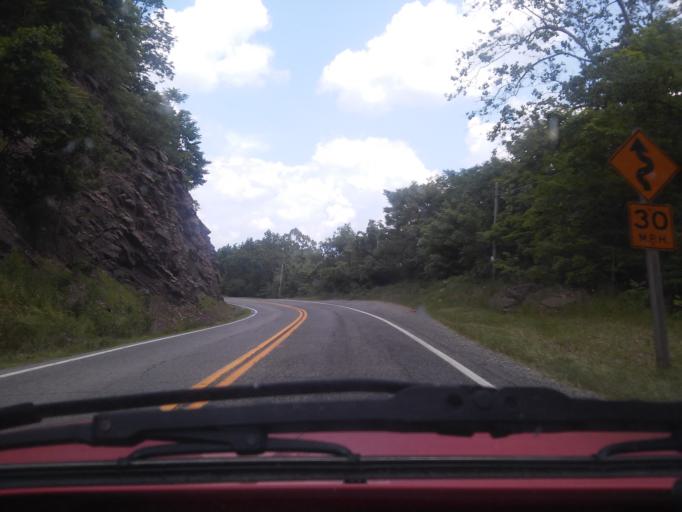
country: US
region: Virginia
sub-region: Craig County
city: New Castle
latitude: 37.4831
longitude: -80.1308
